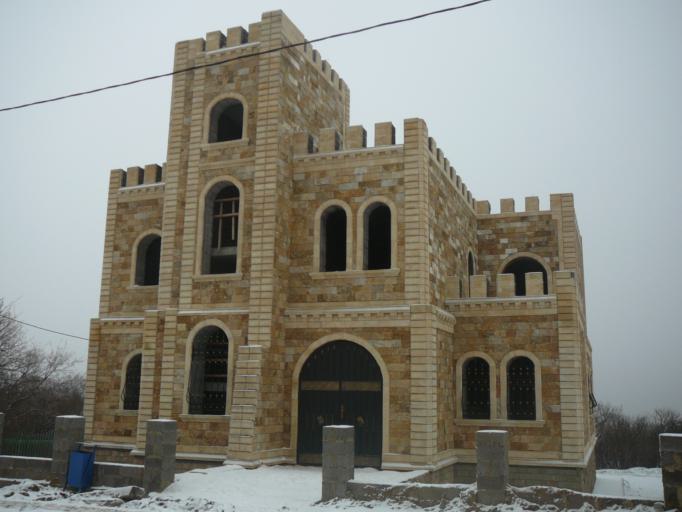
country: RU
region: Saratov
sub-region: Saratovskiy Rayon
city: Saratov
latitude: 51.5408
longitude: 46.0608
